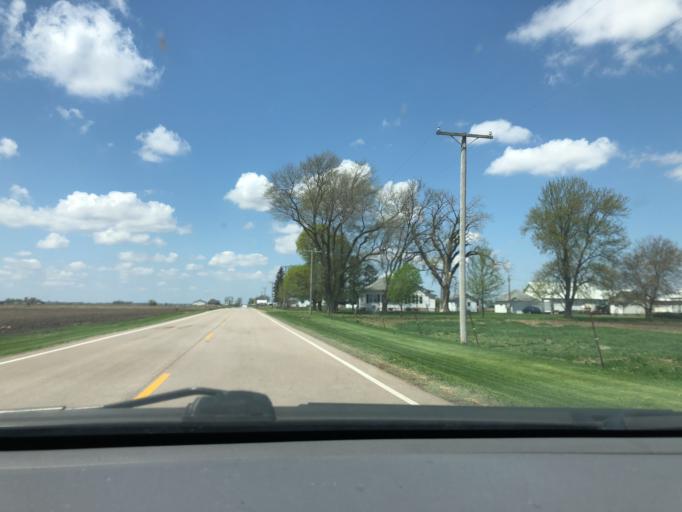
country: US
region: Illinois
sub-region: Kane County
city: Hampshire
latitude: 42.1101
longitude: -88.5809
